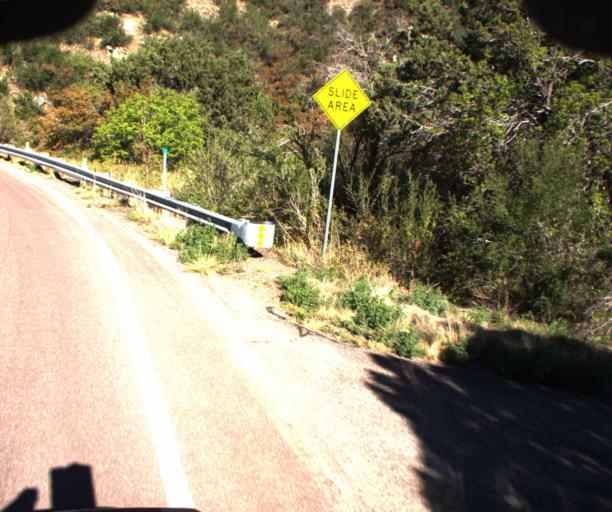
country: US
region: Arizona
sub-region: Yavapai County
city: Prescott
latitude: 34.4755
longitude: -112.5173
